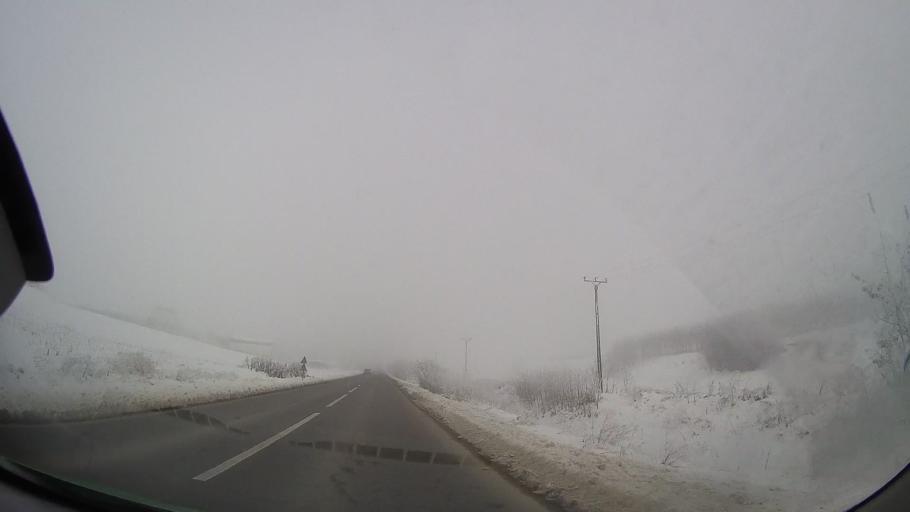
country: RO
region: Iasi
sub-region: Comuna Stolniceni-Prajescu
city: Stolniceni-Prajescu
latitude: 47.1898
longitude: 26.7367
